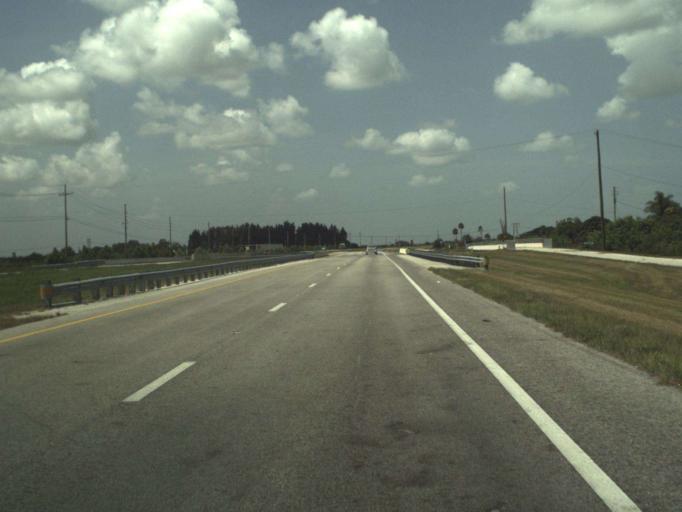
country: US
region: Florida
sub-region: Saint Lucie County
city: Fort Pierce South
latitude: 27.3957
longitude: -80.4577
